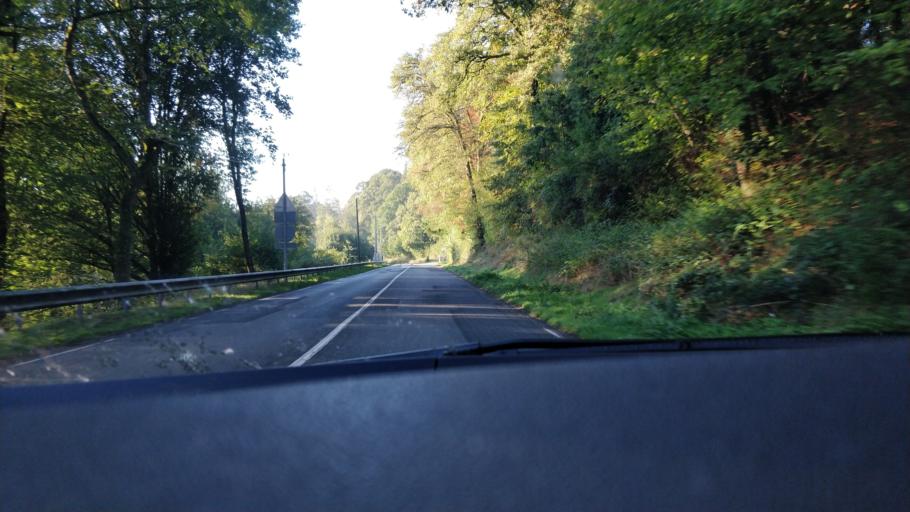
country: FR
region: Limousin
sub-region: Departement de la Creuse
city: Bourganeuf
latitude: 45.9586
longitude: 1.7408
